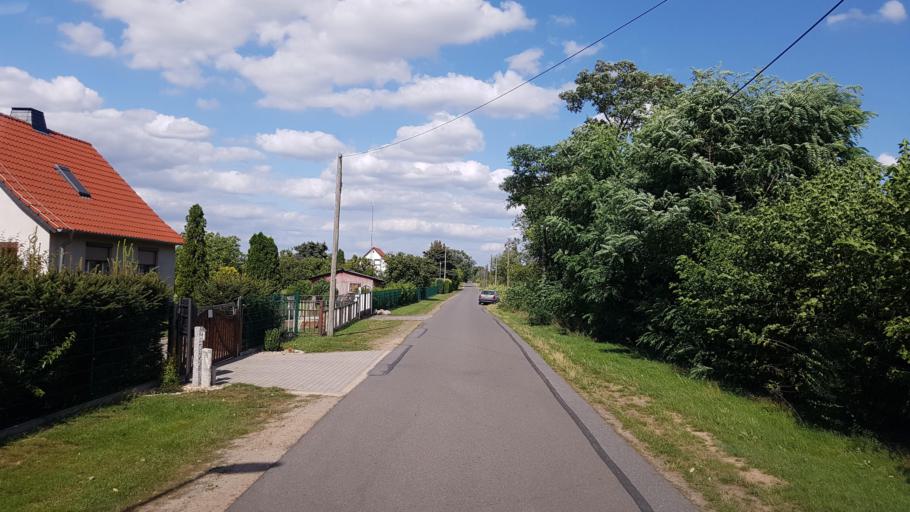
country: DE
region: Brandenburg
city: Muhlberg
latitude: 51.4466
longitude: 13.2926
